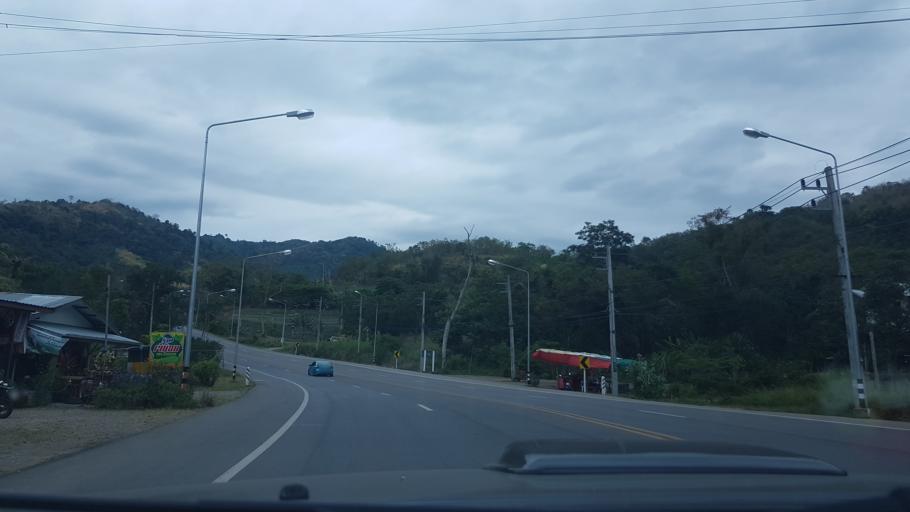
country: TH
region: Phetchabun
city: Khao Kho
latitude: 16.5438
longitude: 101.0524
